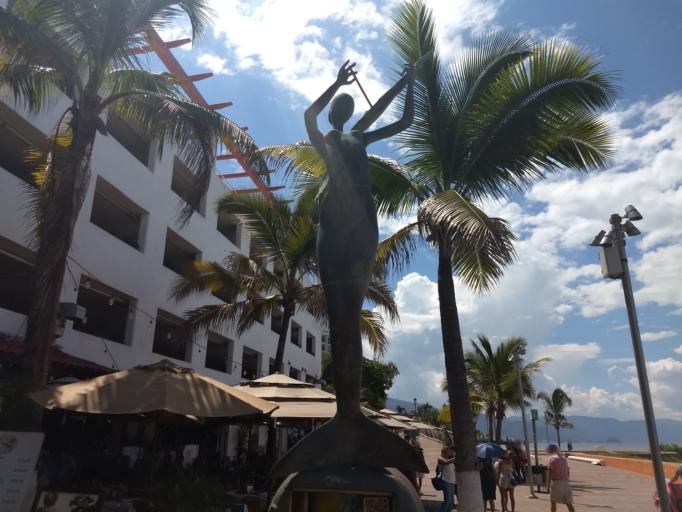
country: MX
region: Jalisco
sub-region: Puerto Vallarta
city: Puerto Vallarta
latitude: 20.6070
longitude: -105.2374
